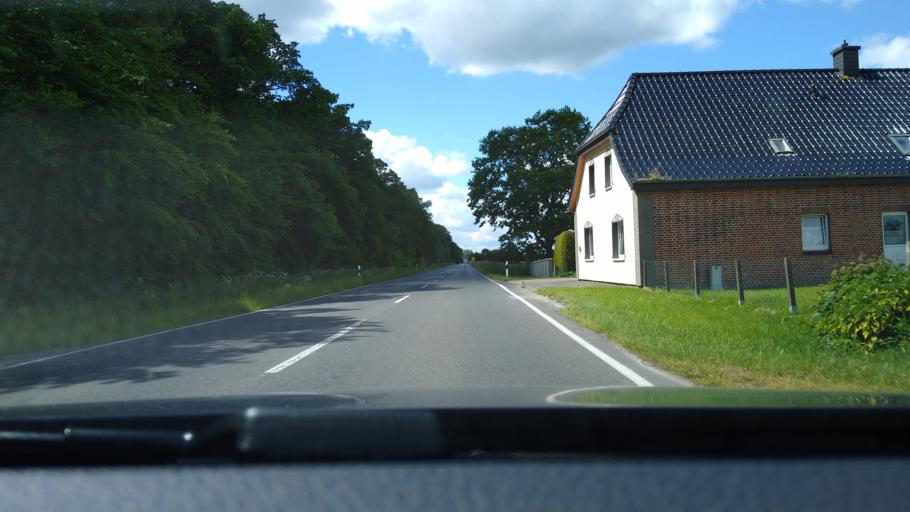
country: DE
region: Schleswig-Holstein
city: Kellenhusen
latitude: 54.2100
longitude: 11.0463
